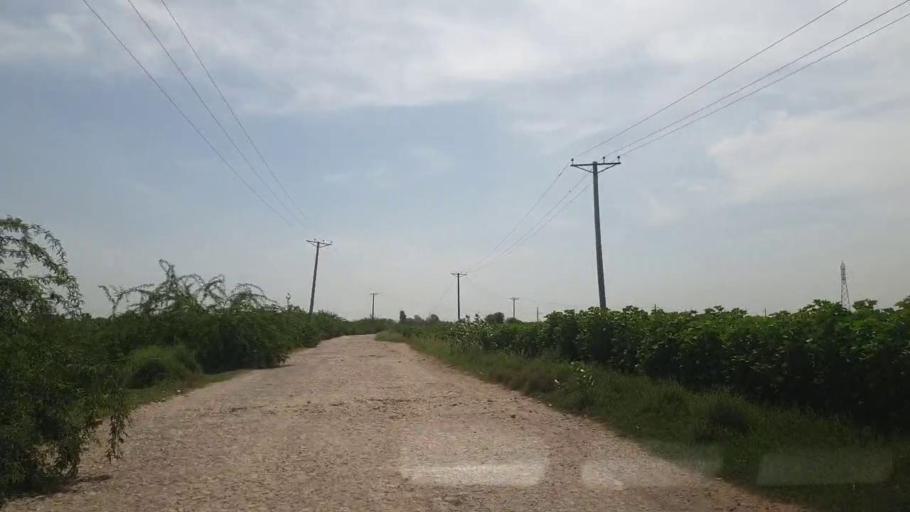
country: PK
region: Sindh
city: Kot Diji
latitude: 27.1289
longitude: 68.9958
